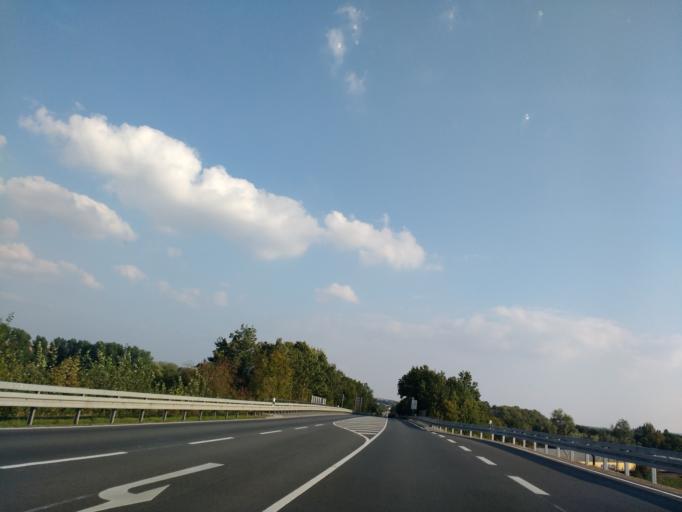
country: DE
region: North Rhine-Westphalia
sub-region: Regierungsbezirk Detmold
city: Steinheim
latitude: 51.8815
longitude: 9.0943
